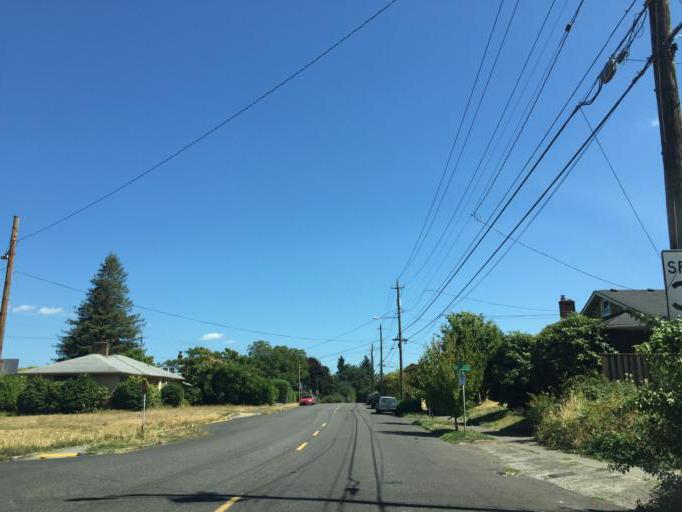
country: US
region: Oregon
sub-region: Multnomah County
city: Portland
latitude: 45.5719
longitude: -122.6330
